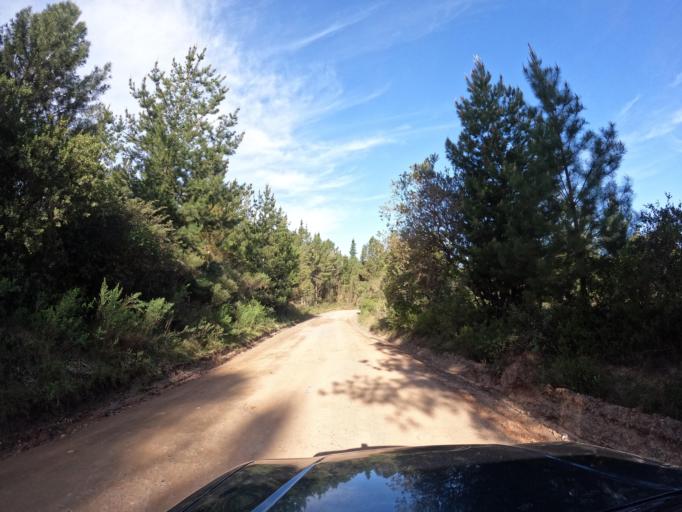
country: CL
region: Biobio
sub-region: Provincia de Biobio
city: La Laja
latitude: -37.1487
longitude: -72.7285
